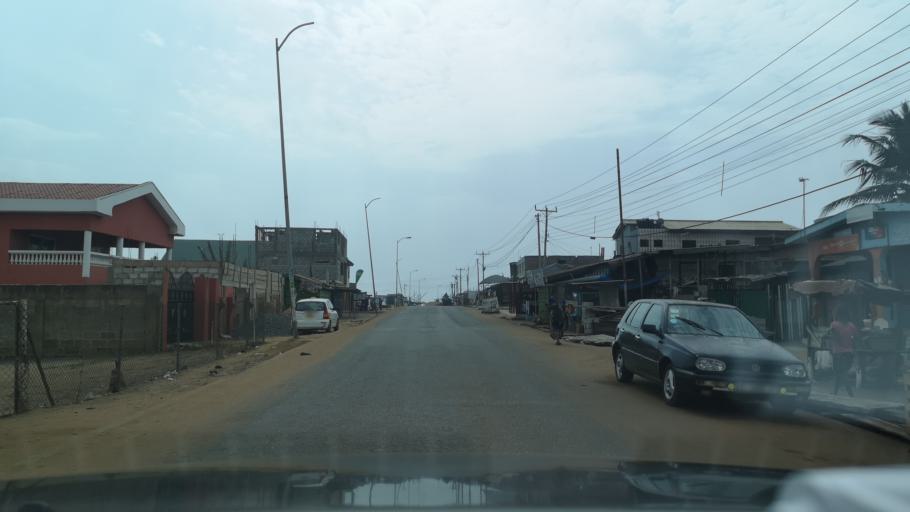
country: GH
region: Greater Accra
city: Nungua
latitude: 5.6141
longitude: -0.0494
